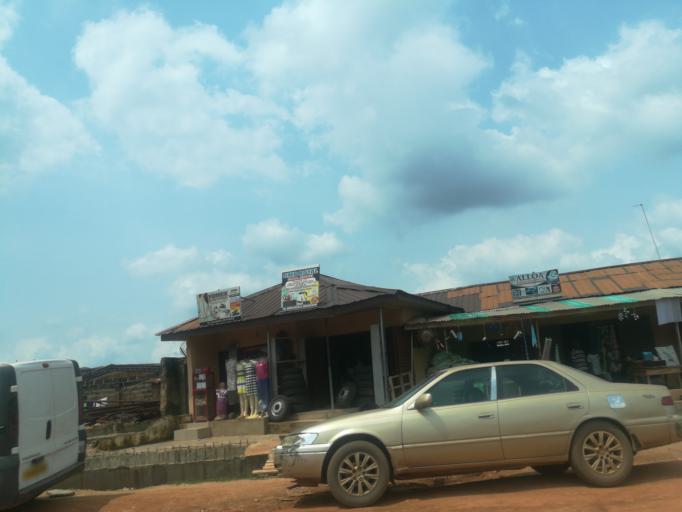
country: NG
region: Oyo
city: Ibadan
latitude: 7.4448
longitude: 3.9515
